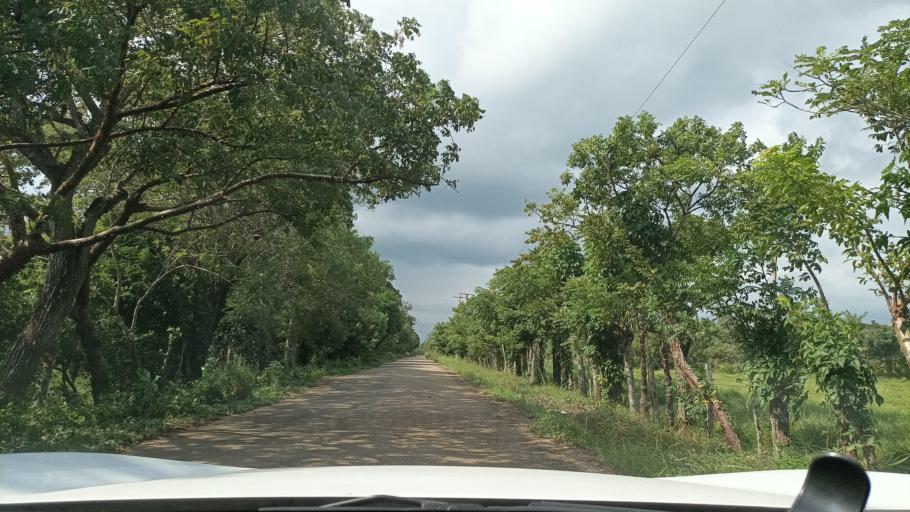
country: MX
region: Veracruz
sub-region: Chinameca
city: Chacalapa
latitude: 18.0813
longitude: -94.6760
